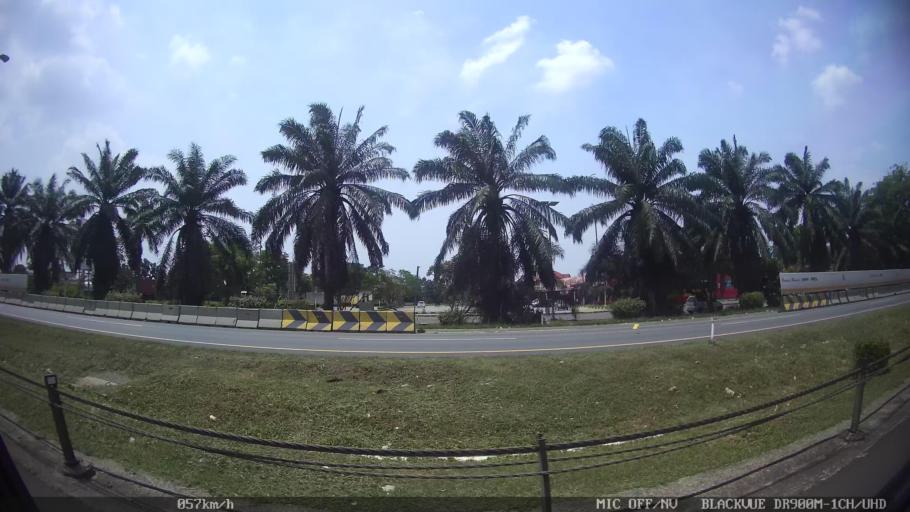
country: ID
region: Banten
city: Serang
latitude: -6.1322
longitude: 106.2043
